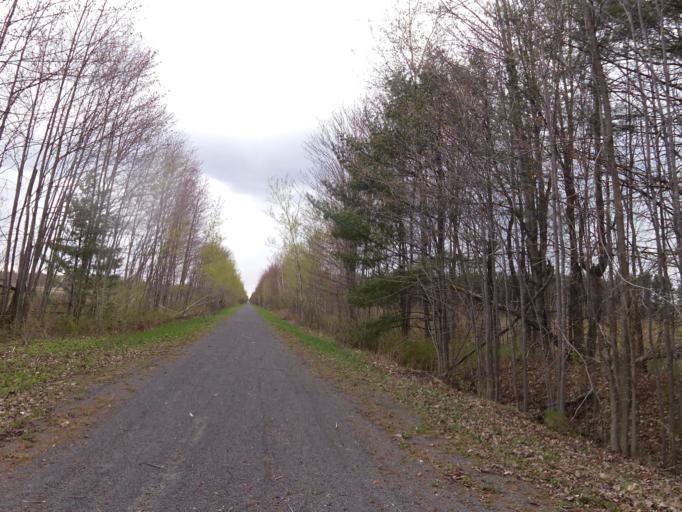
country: CA
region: Ontario
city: Bourget
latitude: 45.4810
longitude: -75.0384
